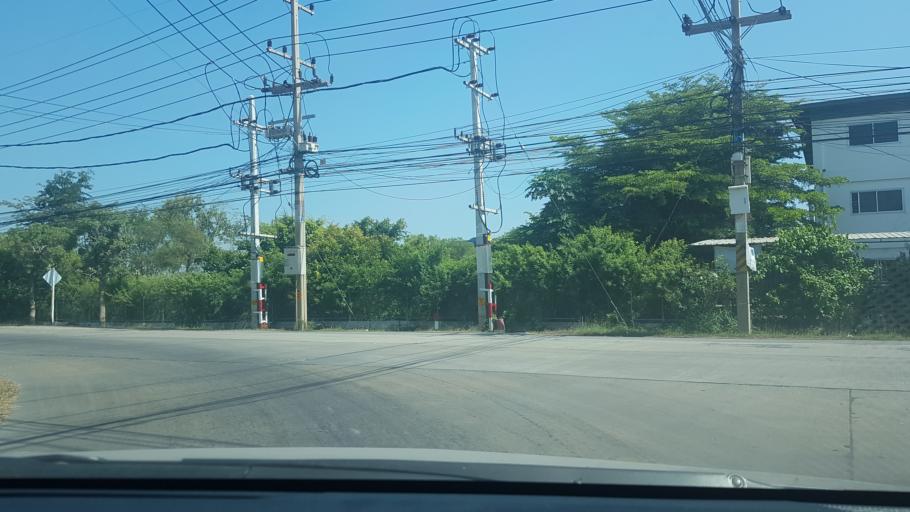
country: TH
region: Phra Nakhon Si Ayutthaya
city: Bang Pa-in
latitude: 14.2474
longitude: 100.6000
